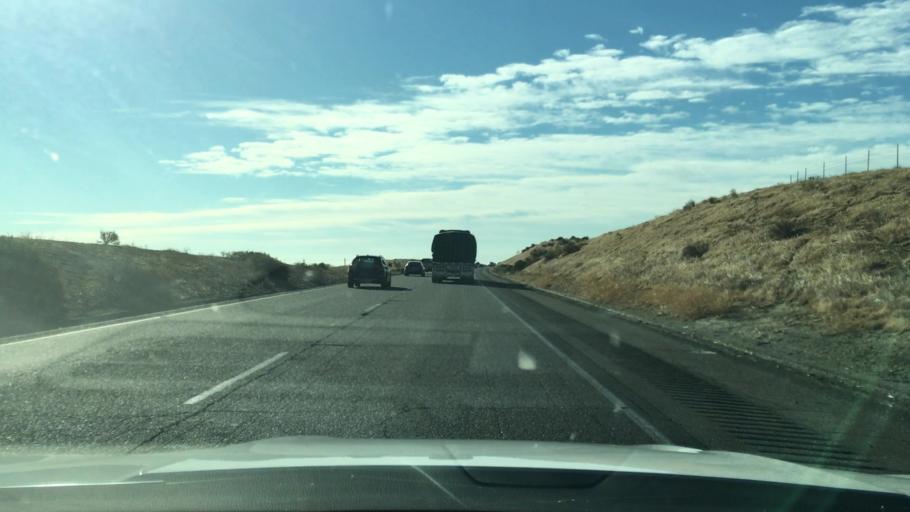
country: US
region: California
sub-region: Fresno County
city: Mendota
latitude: 36.4950
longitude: -120.4494
